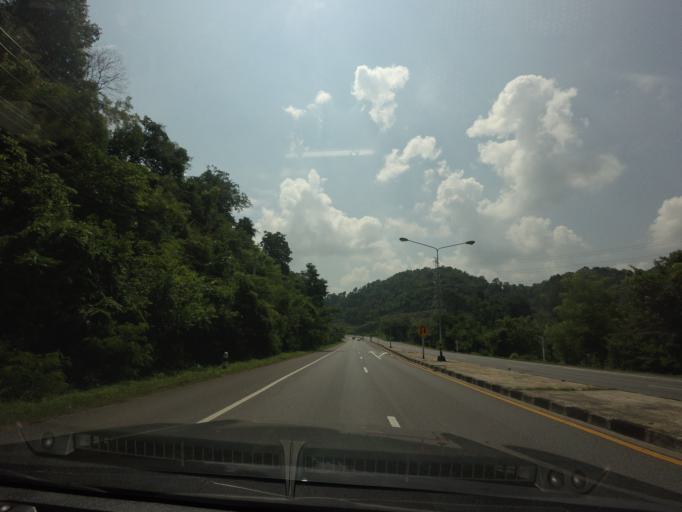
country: TH
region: Uttaradit
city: Uttaradit
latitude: 17.7728
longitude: 100.1316
